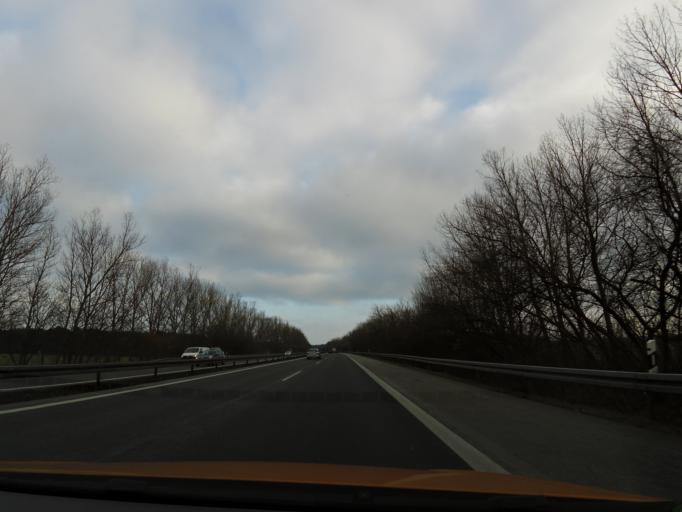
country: DE
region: Brandenburg
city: Fehrbellin
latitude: 52.7760
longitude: 12.8081
